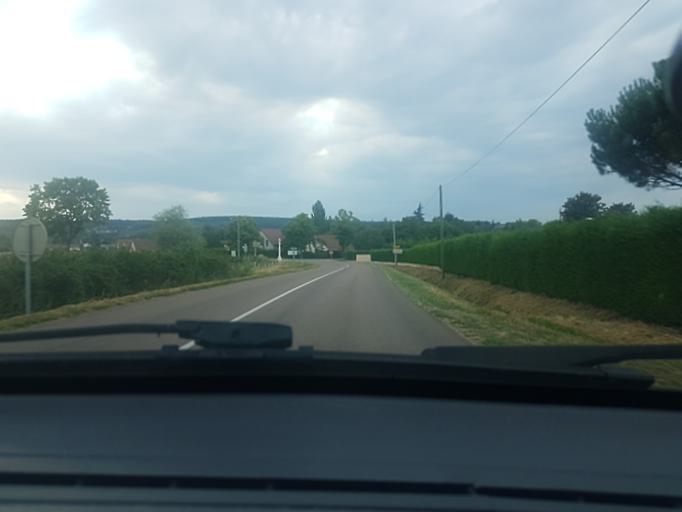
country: FR
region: Bourgogne
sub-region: Departement de Saone-et-Loire
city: Givry
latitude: 46.7669
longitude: 4.7392
